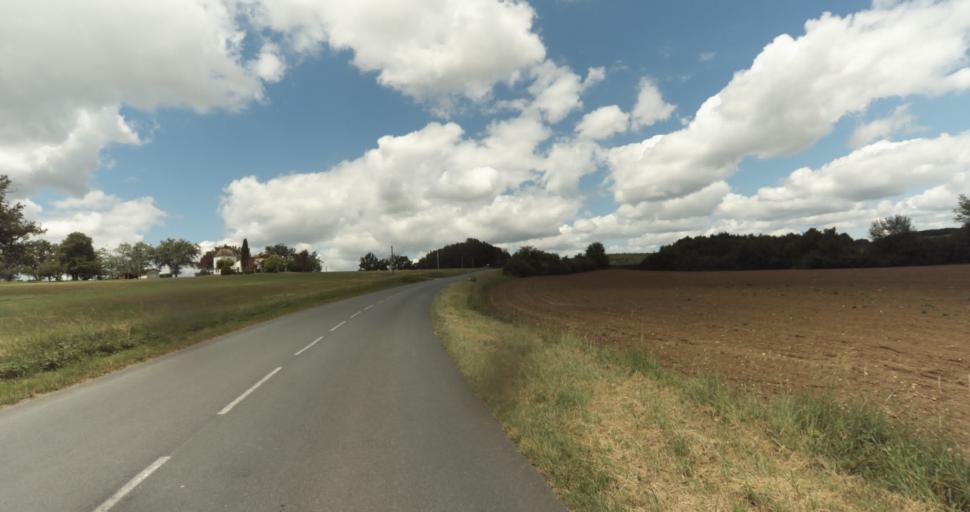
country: FR
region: Aquitaine
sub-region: Departement du Lot-et-Garonne
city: Villereal
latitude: 44.6805
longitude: 0.7614
